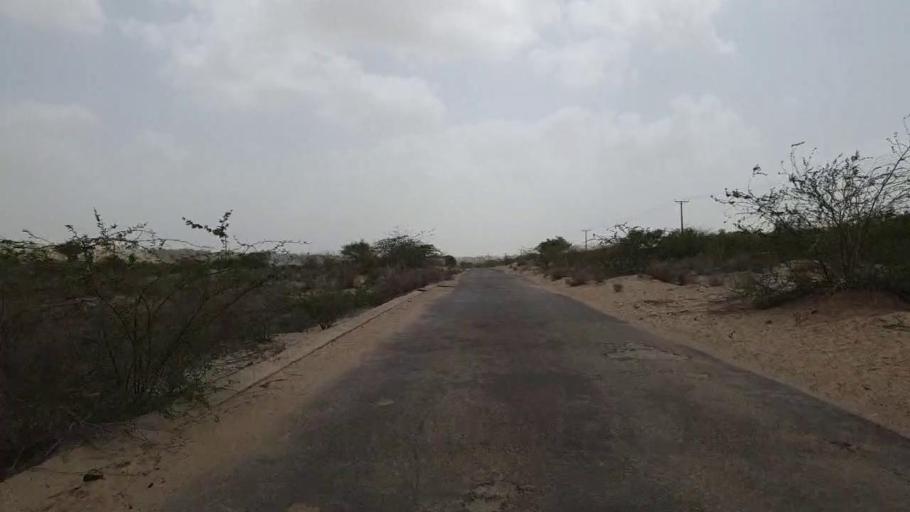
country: PK
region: Sindh
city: Diplo
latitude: 24.4024
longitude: 69.4732
